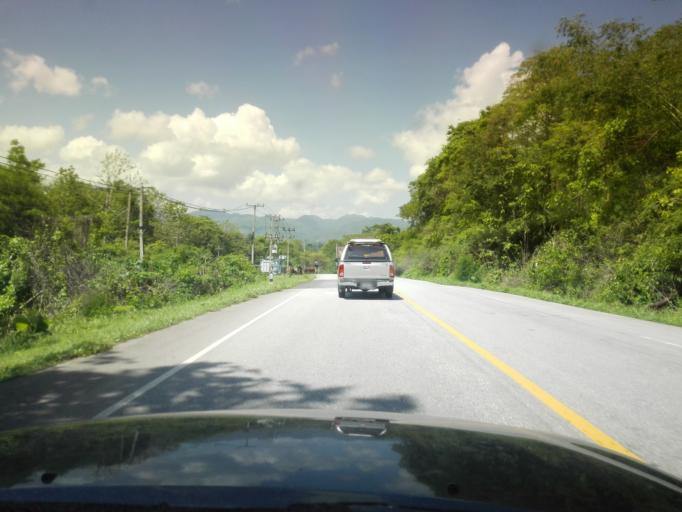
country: TH
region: Tak
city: Mae Sot
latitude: 16.7682
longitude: 98.7801
